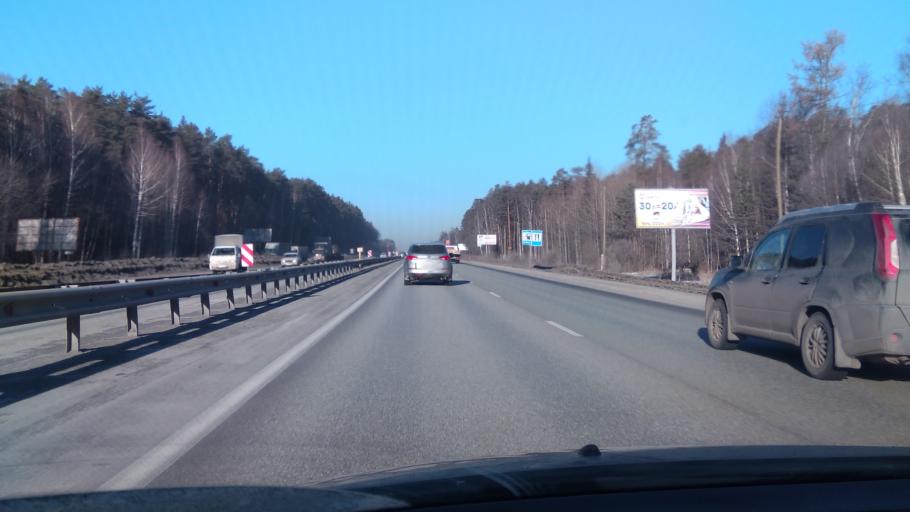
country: RU
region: Sverdlovsk
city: Severka
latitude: 56.8374
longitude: 60.2783
